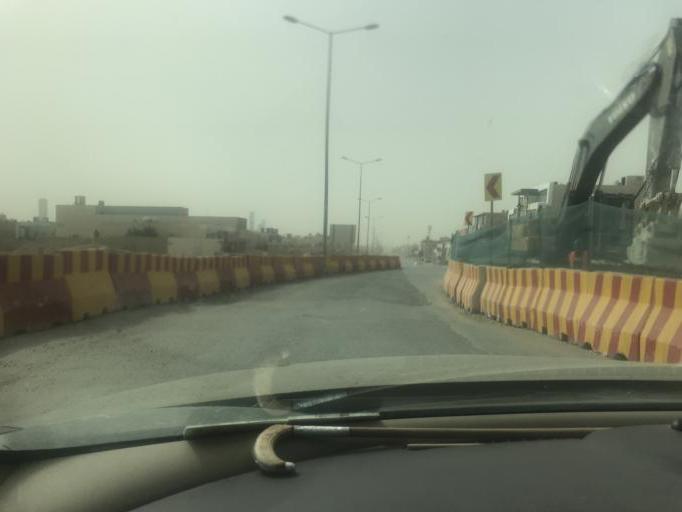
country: SA
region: Ar Riyad
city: Riyadh
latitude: 24.8117
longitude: 46.5999
